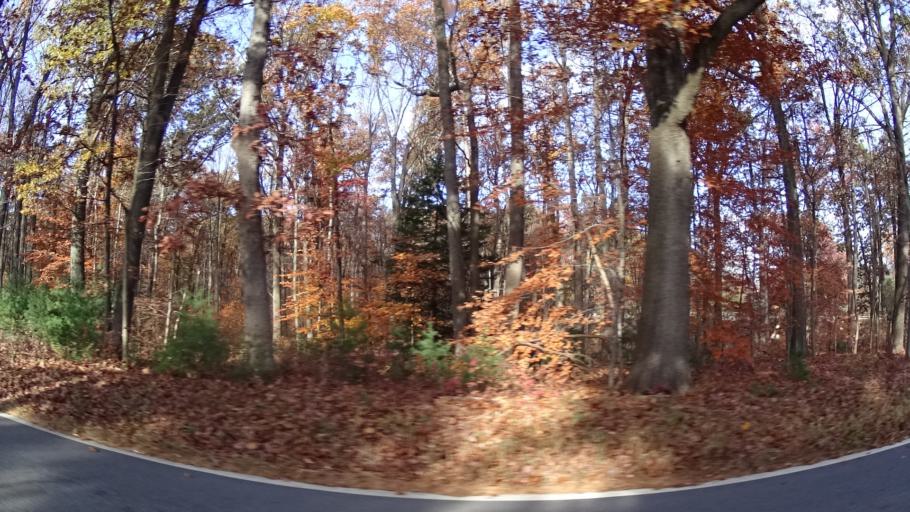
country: US
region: New Jersey
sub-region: Morris County
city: Morristown
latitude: 40.7466
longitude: -74.5057
